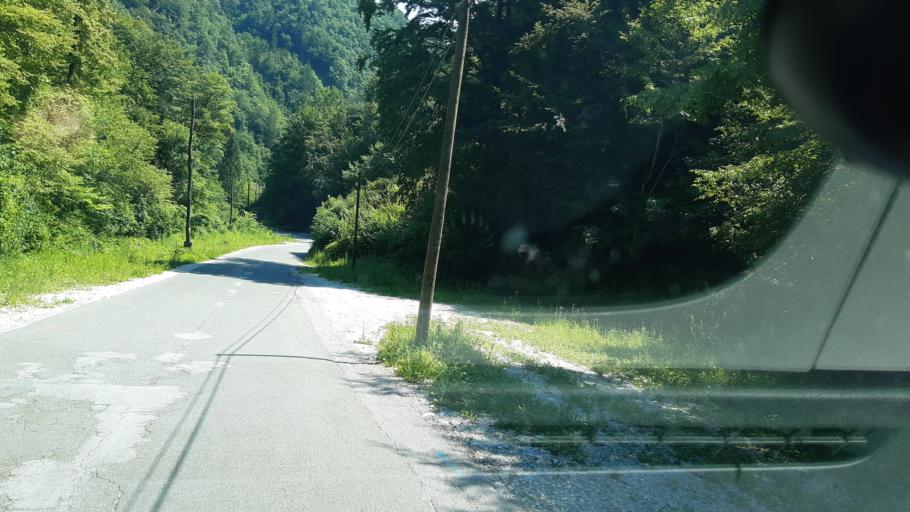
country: SI
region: Cerklje na Gorenjskem
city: Cerklje na Gorenjskem
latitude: 46.2812
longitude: 14.4951
